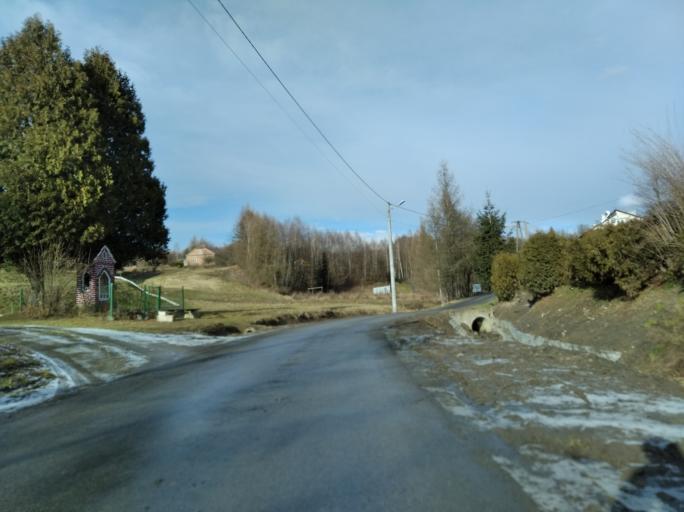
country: PL
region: Subcarpathian Voivodeship
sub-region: Powiat strzyzowski
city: Strzyzow
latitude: 49.8990
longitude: 21.7525
